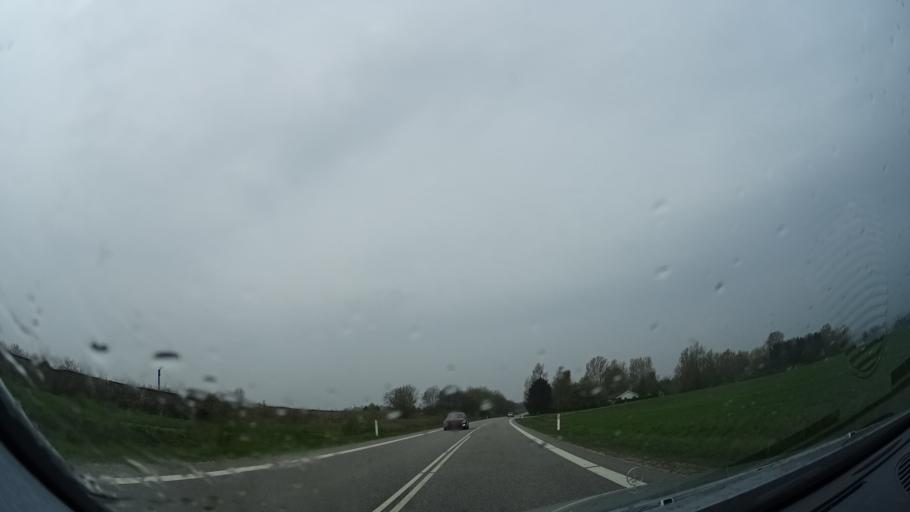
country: DK
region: Zealand
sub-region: Holbaek Kommune
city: Holbaek
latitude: 55.7134
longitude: 11.6598
